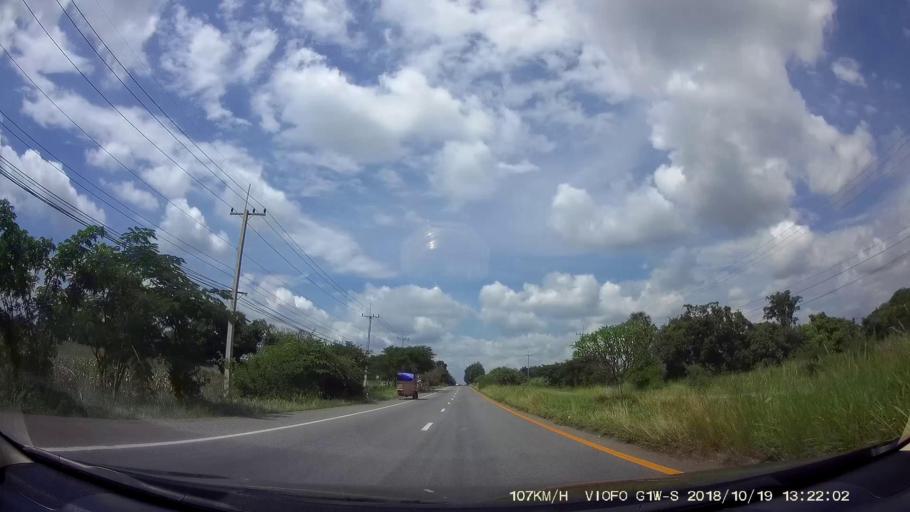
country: TH
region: Chaiyaphum
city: Chatturat
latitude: 15.4712
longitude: 101.8246
